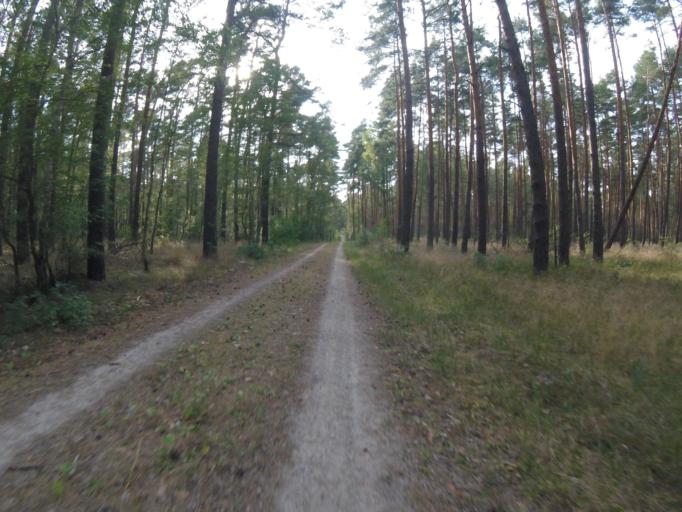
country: DE
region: Brandenburg
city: Gross Koris
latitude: 52.2109
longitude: 13.7332
